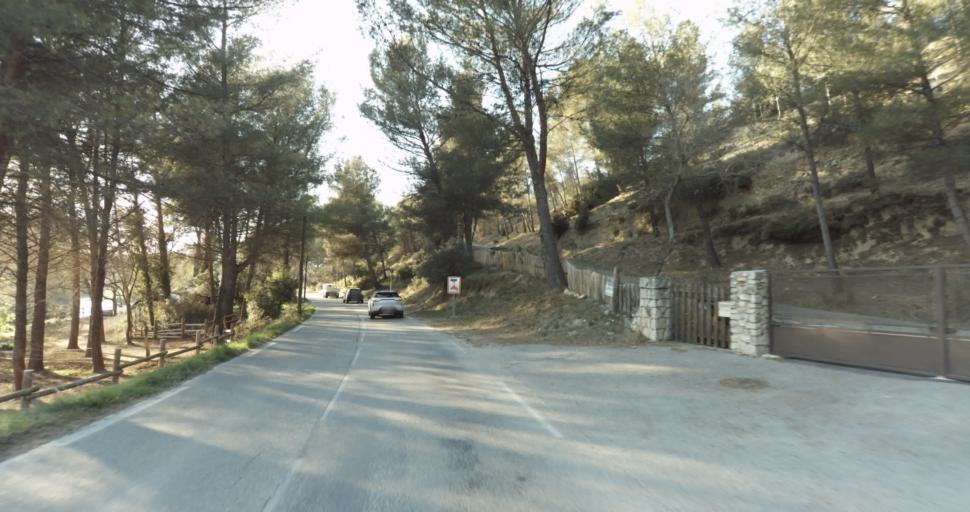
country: FR
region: Provence-Alpes-Cote d'Azur
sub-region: Departement des Bouches-du-Rhone
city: Ventabren
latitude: 43.5264
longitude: 5.2915
